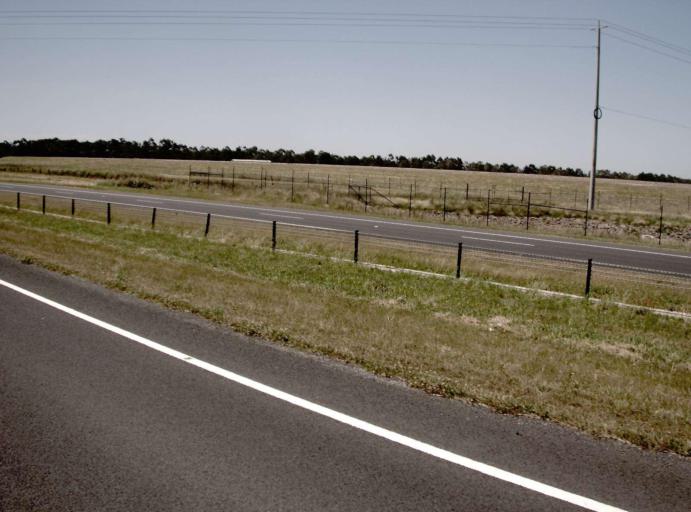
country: AU
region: Victoria
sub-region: Cardinia
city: Pakenham South
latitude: -38.0908
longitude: 145.4974
